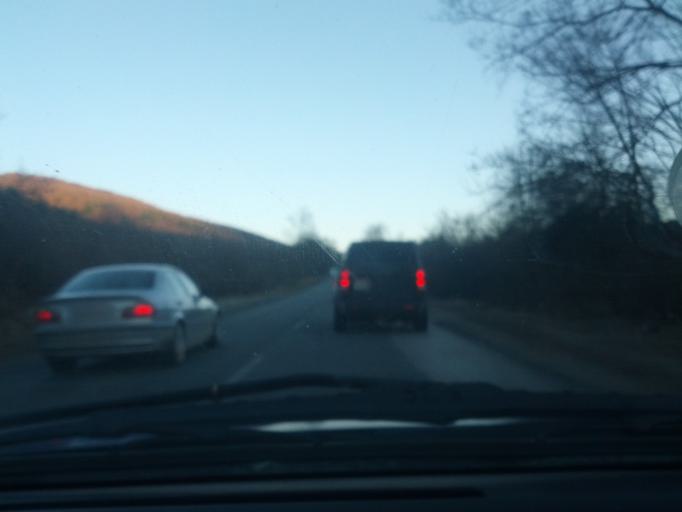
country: BG
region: Vratsa
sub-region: Obshtina Mezdra
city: Mezdra
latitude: 43.0234
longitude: 23.6729
